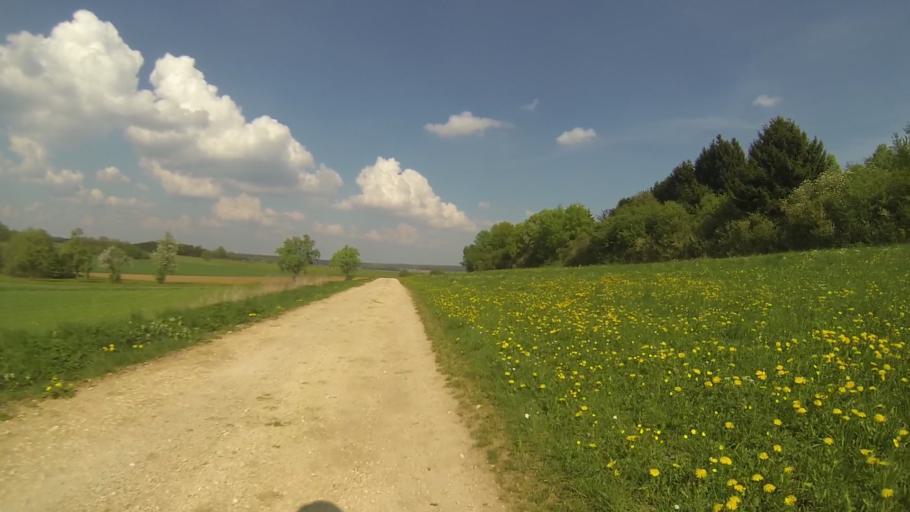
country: DE
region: Baden-Wuerttemberg
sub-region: Regierungsbezirk Stuttgart
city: Gerstetten
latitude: 48.6116
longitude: 10.0409
